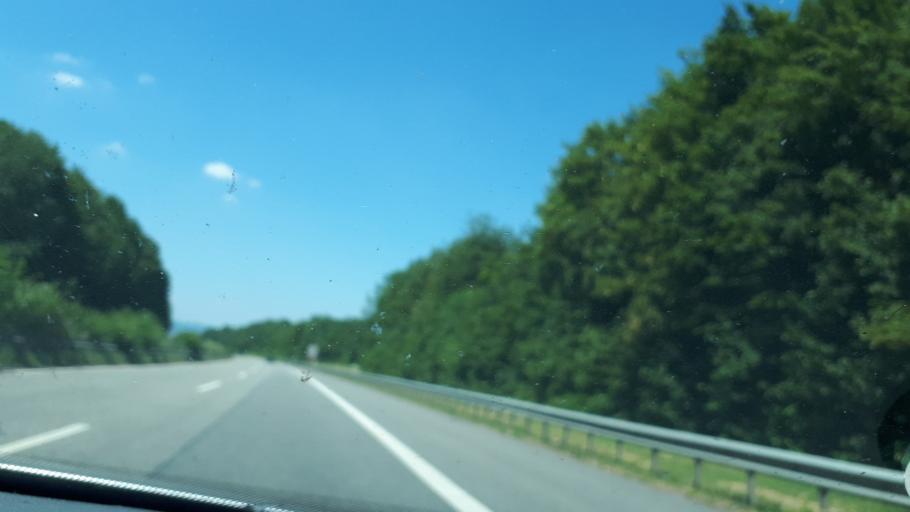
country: DE
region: Rheinland-Pfalz
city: Ochtendung
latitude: 50.3283
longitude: 7.3937
